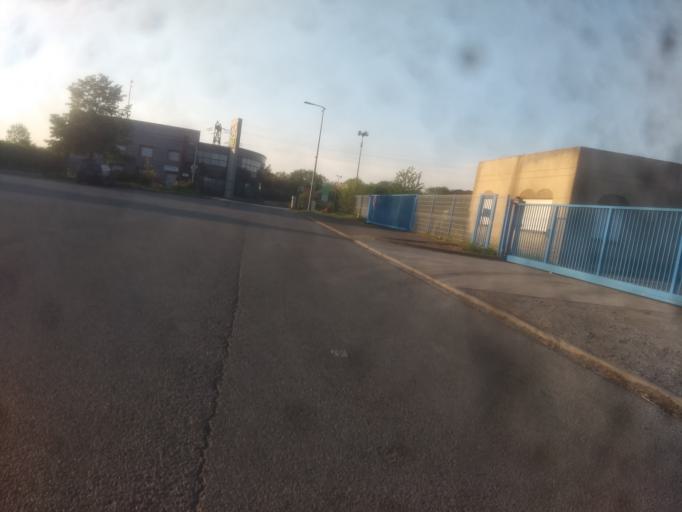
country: FR
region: Nord-Pas-de-Calais
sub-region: Departement du Pas-de-Calais
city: Saint-Laurent-Blangy
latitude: 50.2921
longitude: 2.8172
